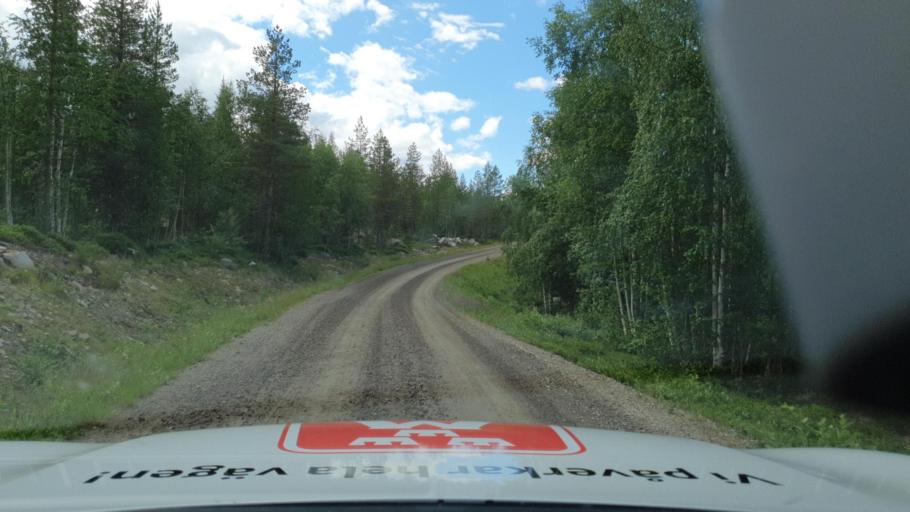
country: SE
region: Vaesterbotten
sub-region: Sorsele Kommun
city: Sorsele
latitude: 65.6662
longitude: 17.3308
